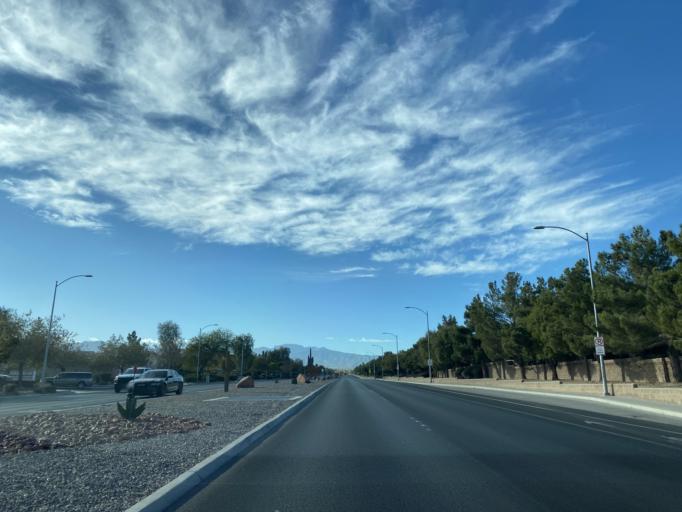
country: US
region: Nevada
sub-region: Clark County
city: North Las Vegas
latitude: 36.3052
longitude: -115.2604
